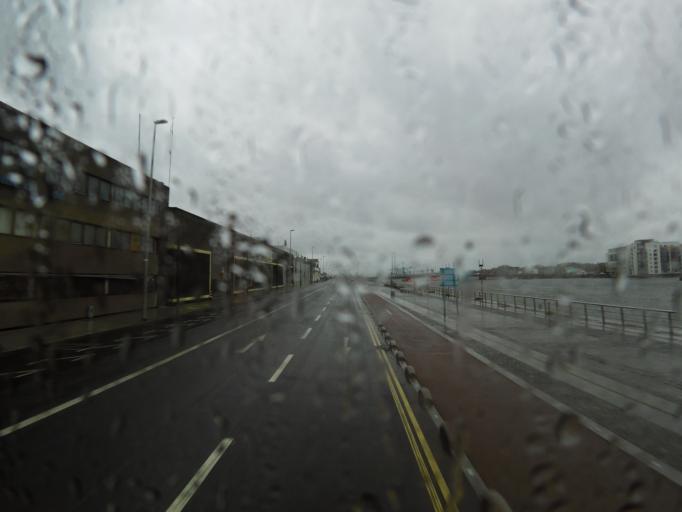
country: IE
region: Leinster
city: Ringsend
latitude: 53.3470
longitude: -6.2319
